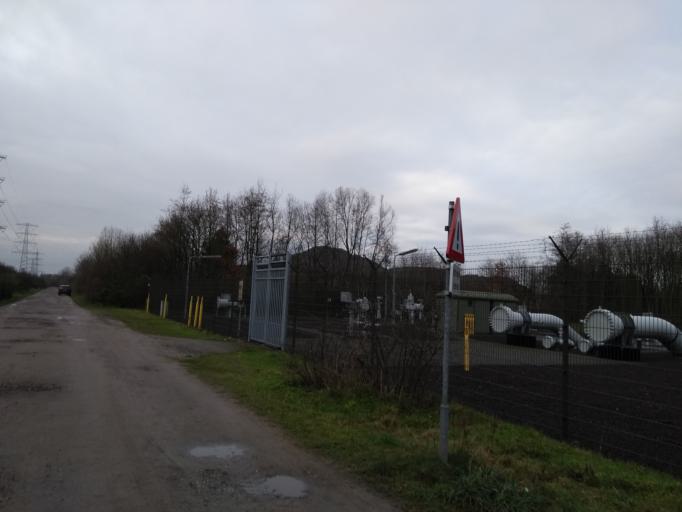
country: NL
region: Overijssel
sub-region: Gemeente Hengelo
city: Hengelo
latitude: 52.2229
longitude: 6.7960
